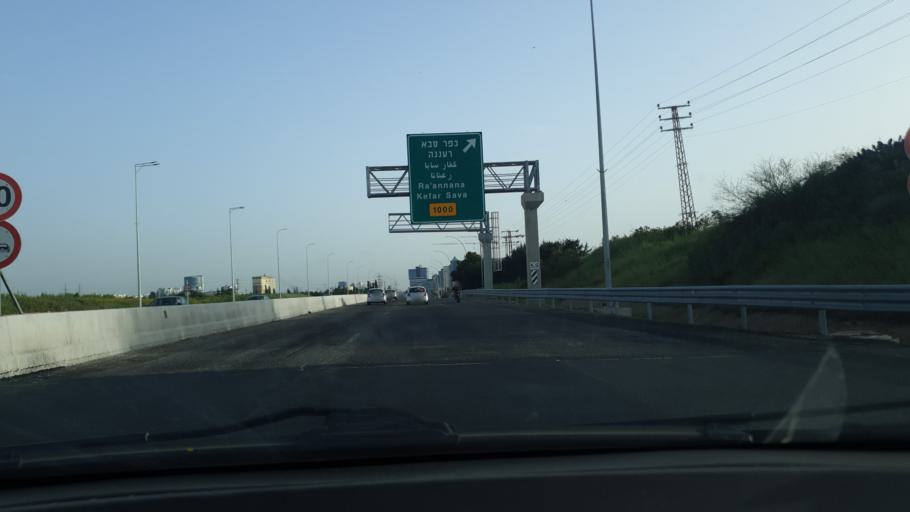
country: IL
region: Central District
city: Ra'anana
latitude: 32.2081
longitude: 34.8838
